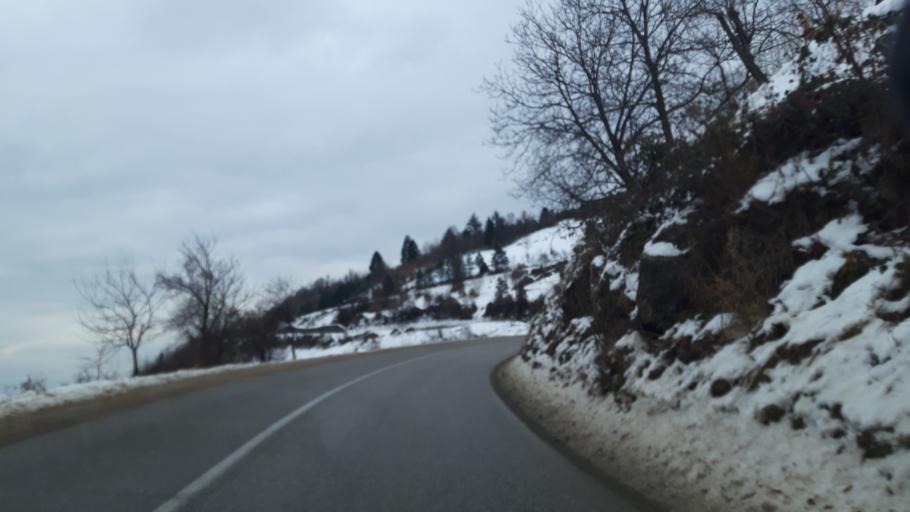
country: BA
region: Republika Srpska
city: Vlasenica
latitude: 44.1804
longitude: 18.9470
